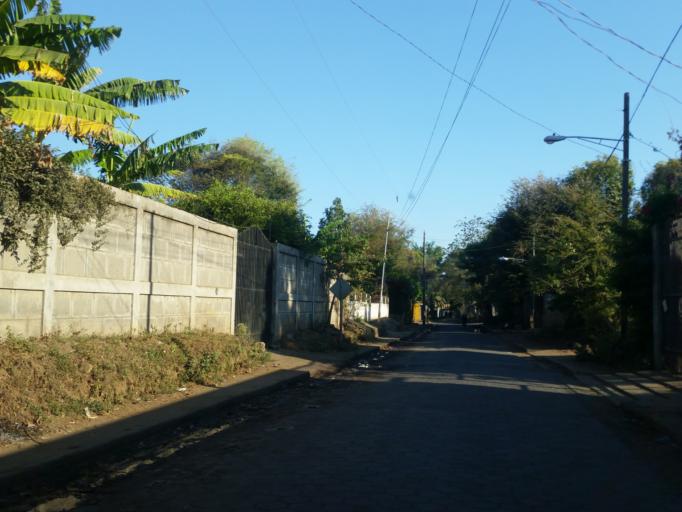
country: NI
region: Masaya
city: Ticuantepe
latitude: 12.0710
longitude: -86.2142
